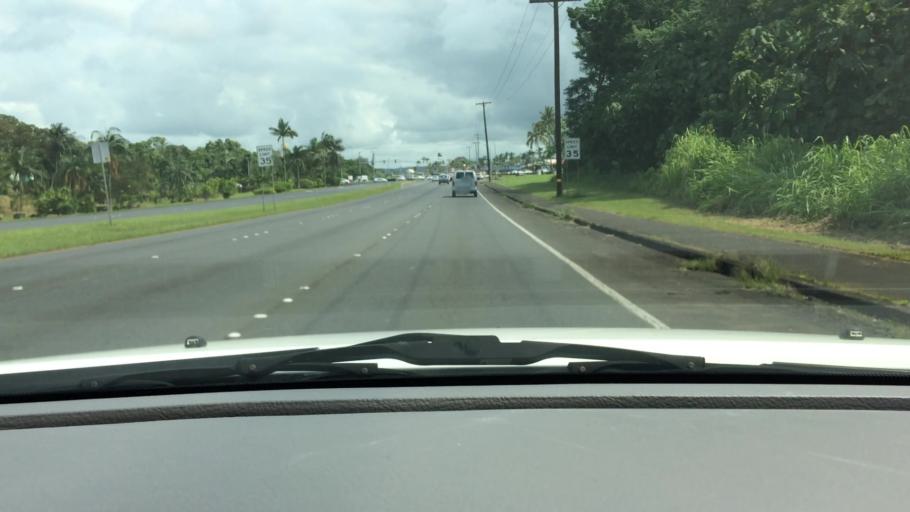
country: US
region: Hawaii
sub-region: Hawaii County
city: Hilo
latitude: 19.6976
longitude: -155.0654
